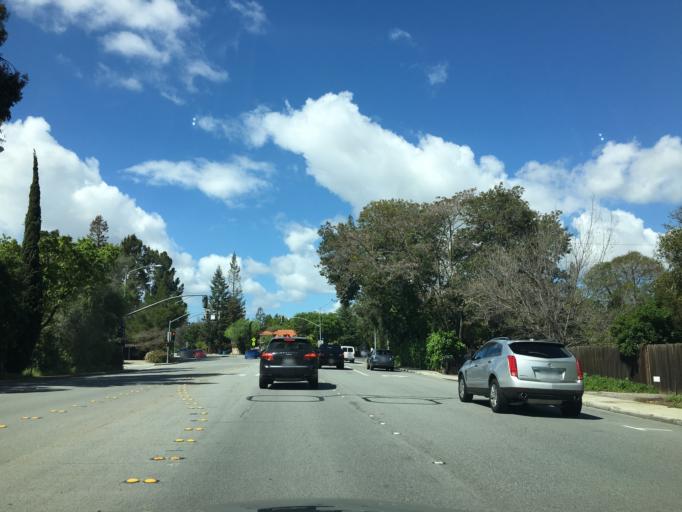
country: US
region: California
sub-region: San Mateo County
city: West Menlo Park
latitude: 37.4282
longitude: -122.1953
